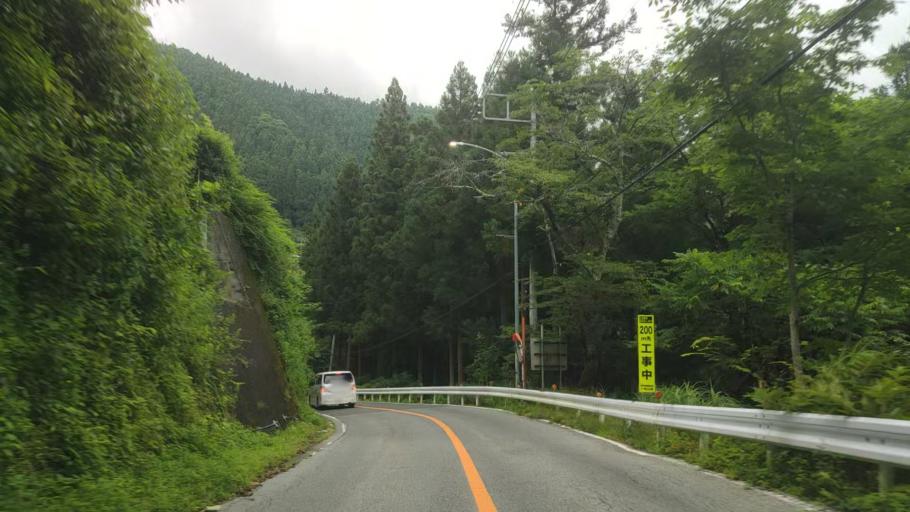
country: JP
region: Saitama
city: Chichibu
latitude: 35.9460
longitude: 138.9120
